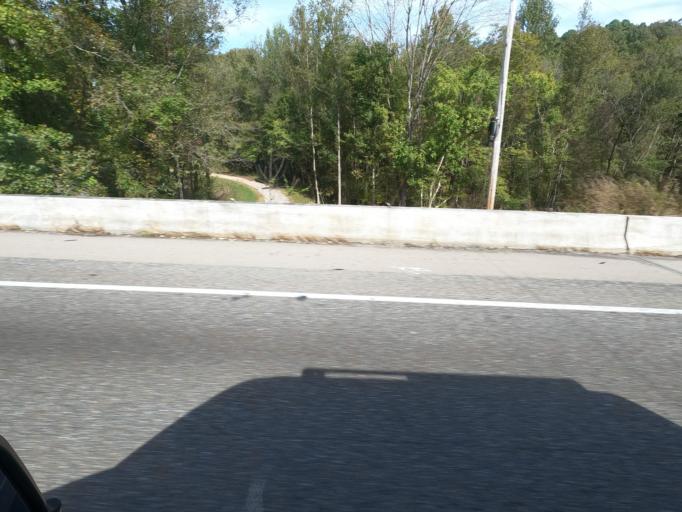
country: US
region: Tennessee
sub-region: Humphreys County
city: New Johnsonville
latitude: 35.8818
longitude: -87.8392
